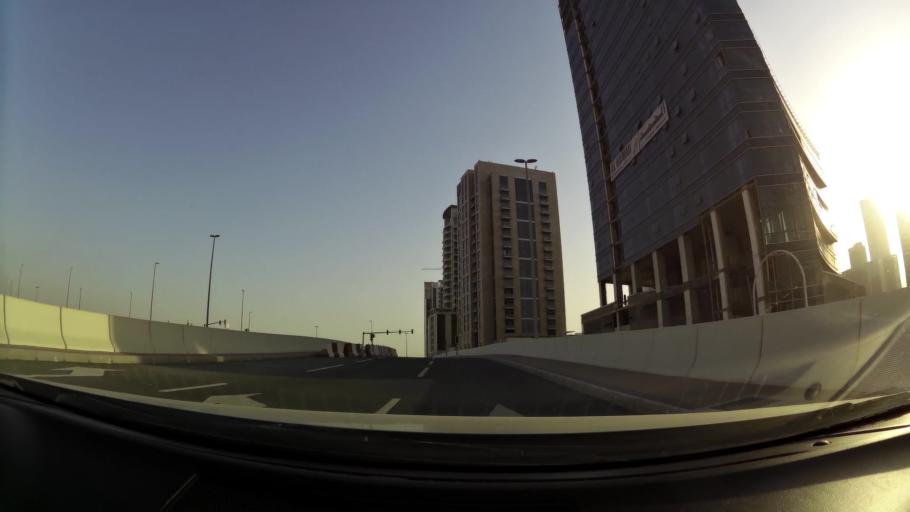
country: AE
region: Dubai
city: Dubai
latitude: 25.1866
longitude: 55.2872
